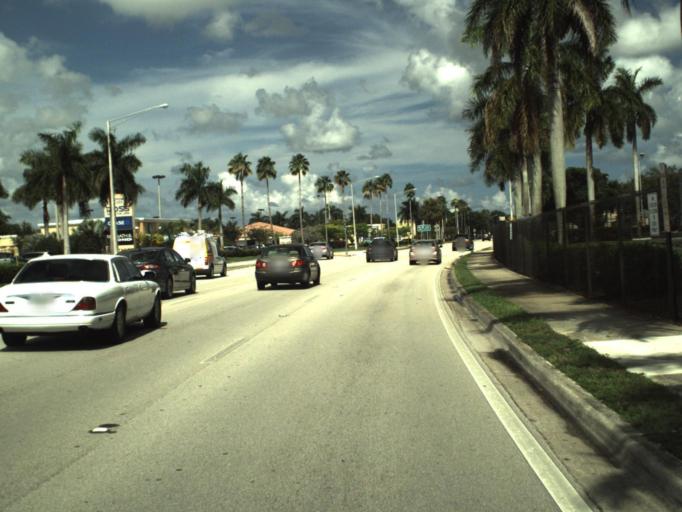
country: US
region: Florida
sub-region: Broward County
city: Pembroke Pines
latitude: 26.0324
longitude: -80.1992
